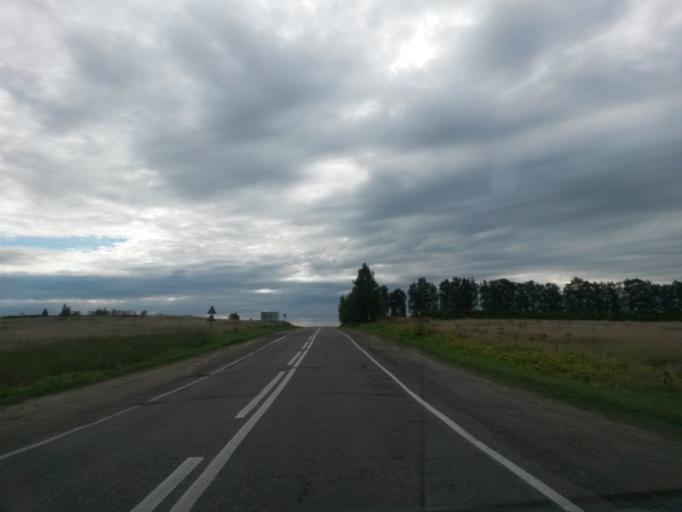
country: RU
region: Jaroslavl
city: Gavrilov-Yam
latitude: 57.3600
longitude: 39.7718
